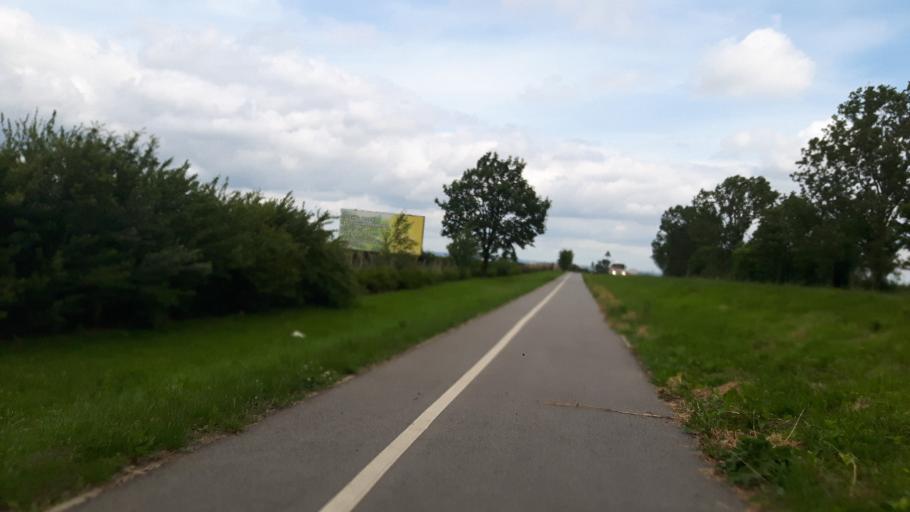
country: PL
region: West Pomeranian Voivodeship
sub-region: Powiat policki
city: Przeclaw
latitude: 53.3563
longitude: 14.4632
